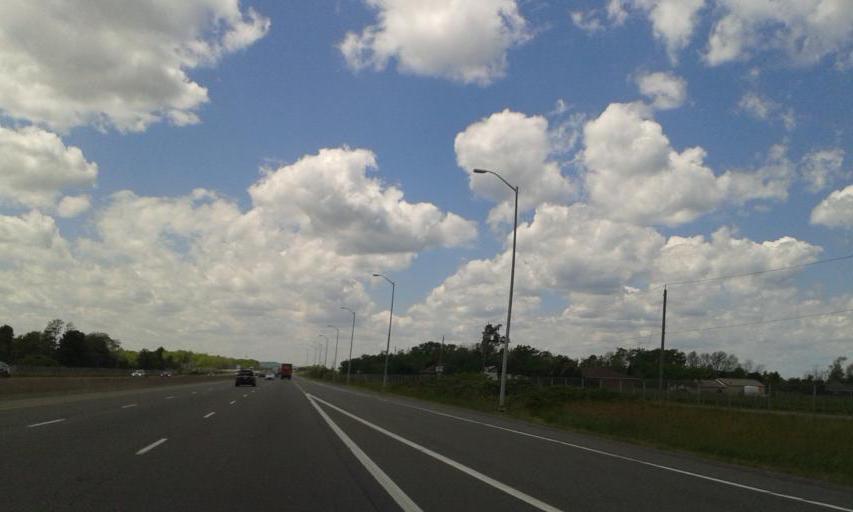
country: CA
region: Ontario
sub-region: Regional Municipality of Niagara
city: St. Catharines
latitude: 43.1875
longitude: -79.4256
